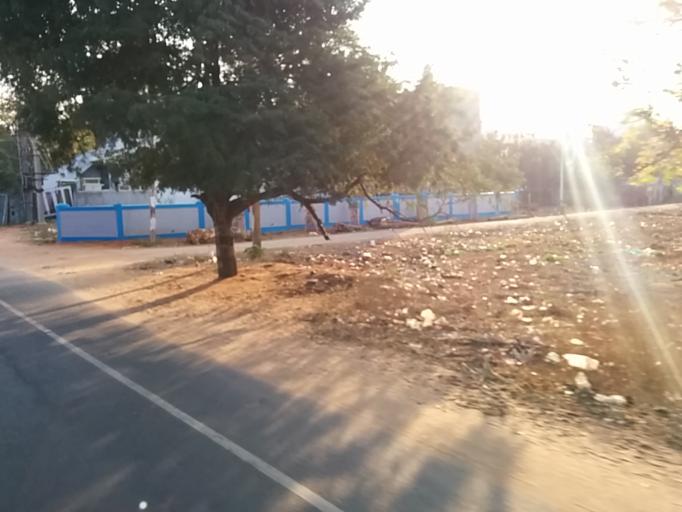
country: IN
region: Tamil Nadu
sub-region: Villupuram
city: Auroville
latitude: 11.9861
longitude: 79.8465
